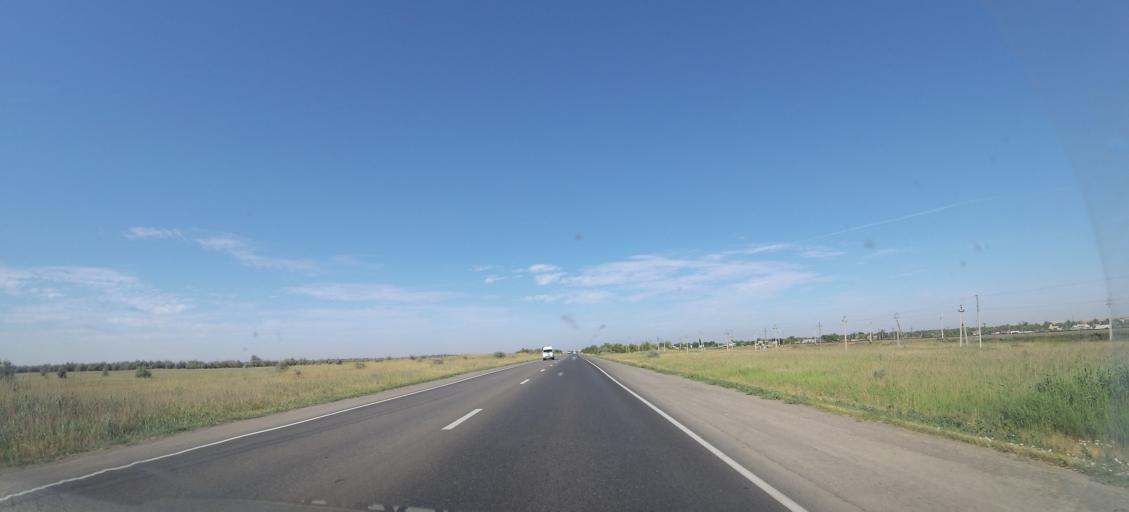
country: RU
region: Volgograd
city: Oktyabr'skiy
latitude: 48.6819
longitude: 43.9178
